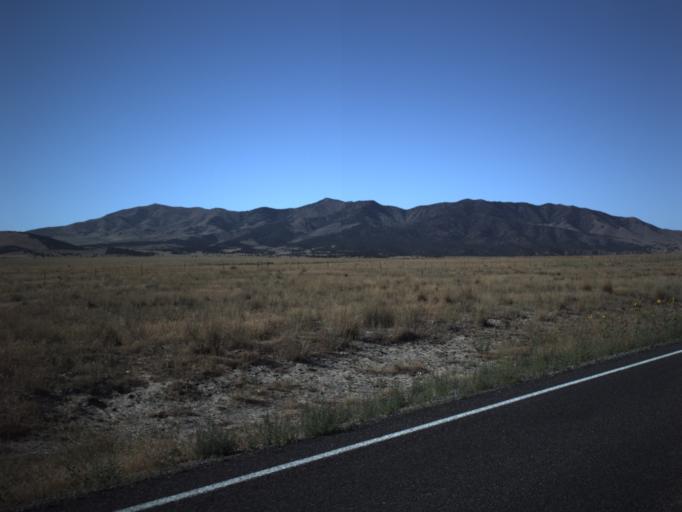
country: US
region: Utah
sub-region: Juab County
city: Mona
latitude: 39.7021
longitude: -112.2177
